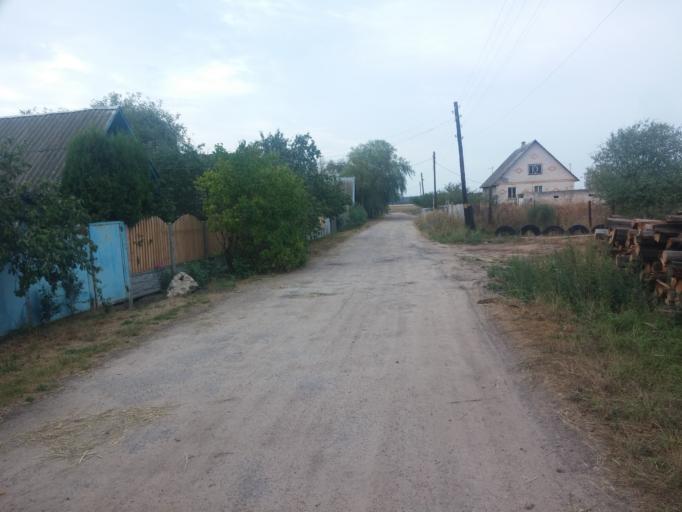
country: BY
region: Minsk
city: Chervyen'
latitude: 53.7806
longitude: 28.2689
